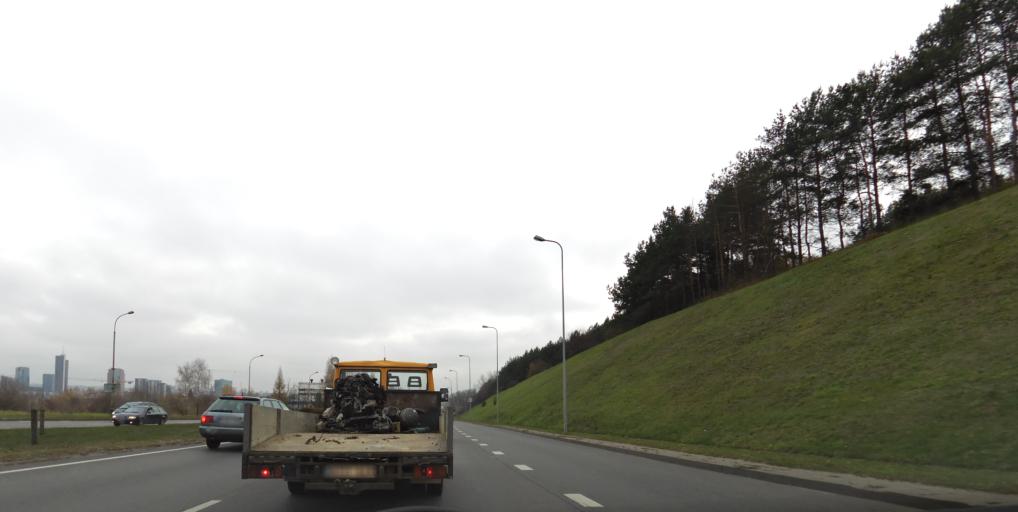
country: LT
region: Vilnius County
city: Seskine
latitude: 54.7111
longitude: 25.2696
